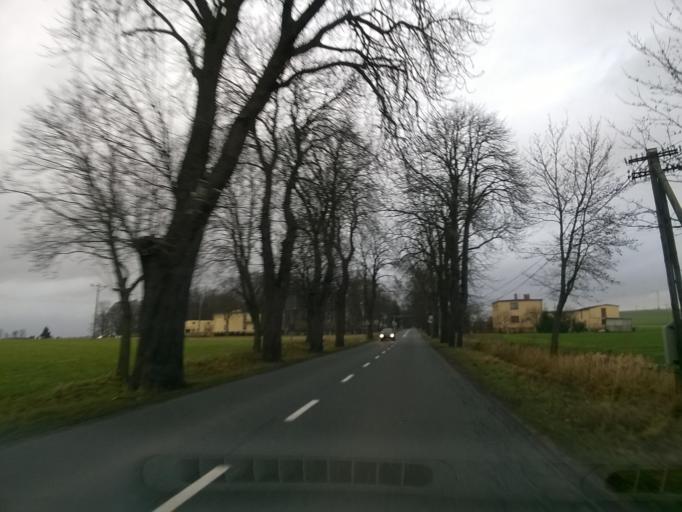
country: PL
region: Kujawsko-Pomorskie
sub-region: Powiat nakielski
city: Kcynia
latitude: 52.9814
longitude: 17.4636
